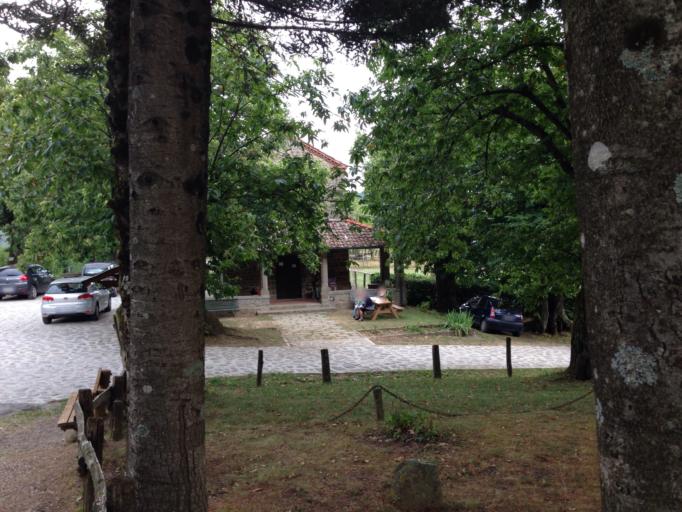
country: IT
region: Tuscany
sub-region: Provincia di Prato
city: Cantagallo
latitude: 44.0699
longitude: 11.0928
